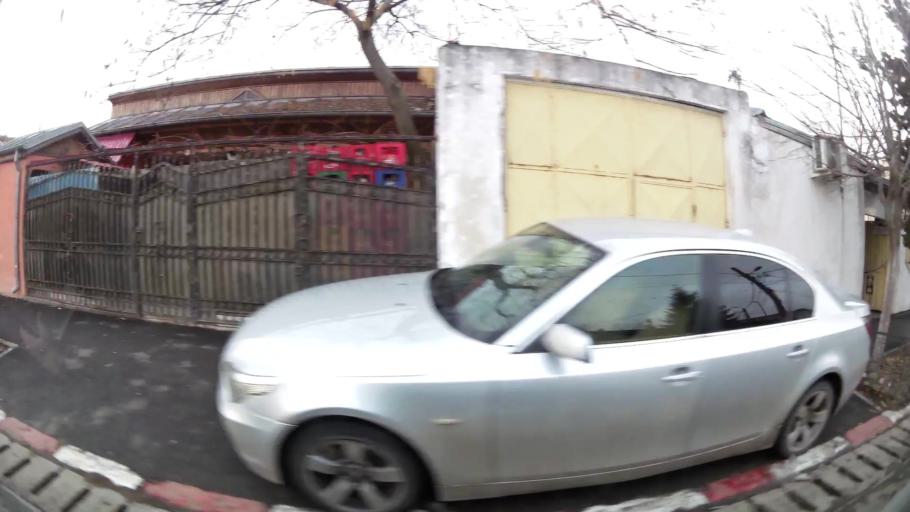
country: RO
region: Ilfov
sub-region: Voluntari City
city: Voluntari
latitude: 44.4838
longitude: 26.1837
